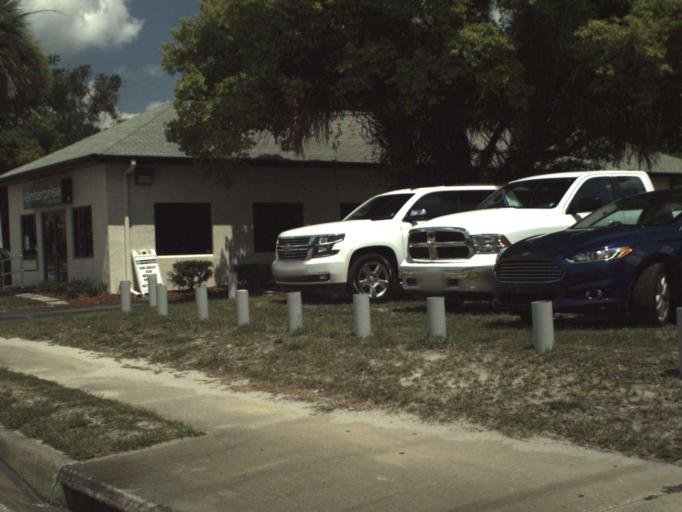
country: US
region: Florida
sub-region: Seminole County
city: Longwood
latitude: 28.6979
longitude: -81.3423
